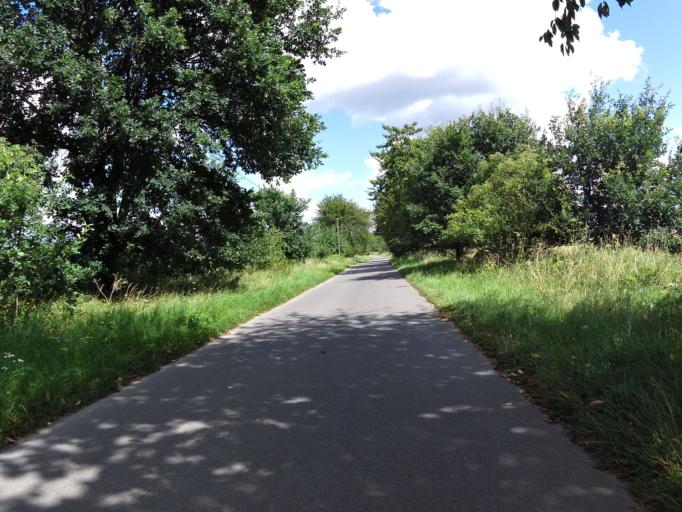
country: DE
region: Brandenburg
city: Lychen
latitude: 53.2798
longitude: 13.4503
